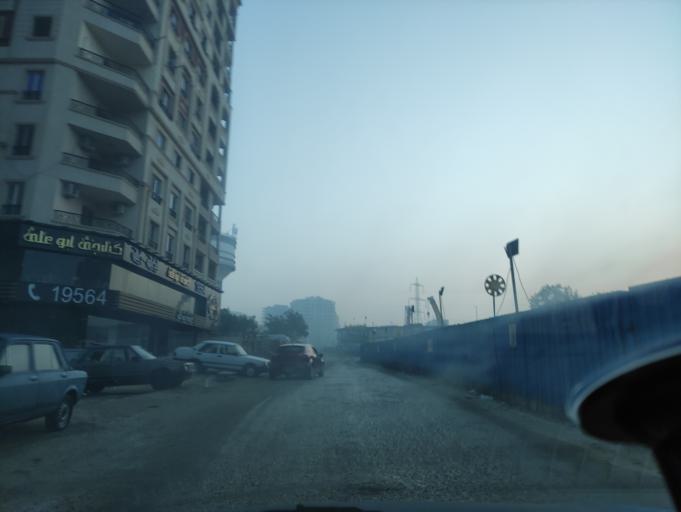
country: EG
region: Muhafazat al Qahirah
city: Cairo
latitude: 30.0474
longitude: 31.3632
